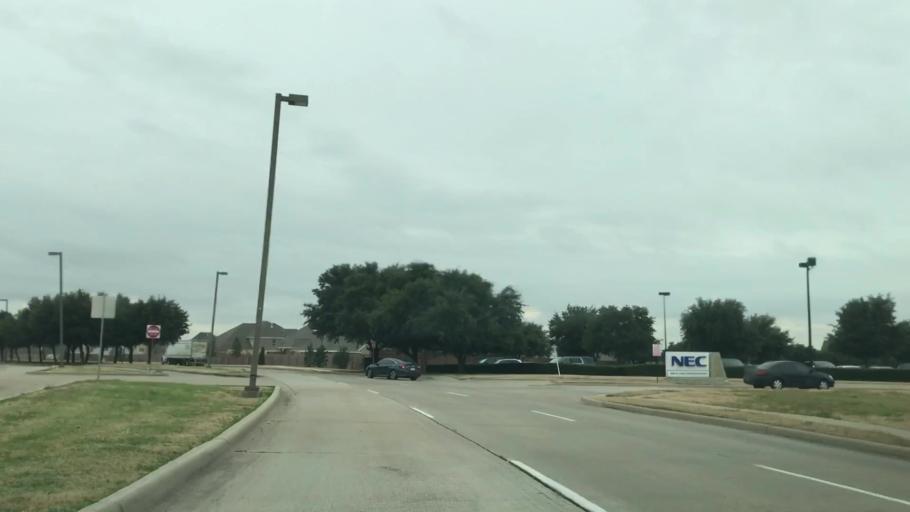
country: US
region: Texas
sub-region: Dallas County
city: Coppell
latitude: 32.9138
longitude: -96.9987
